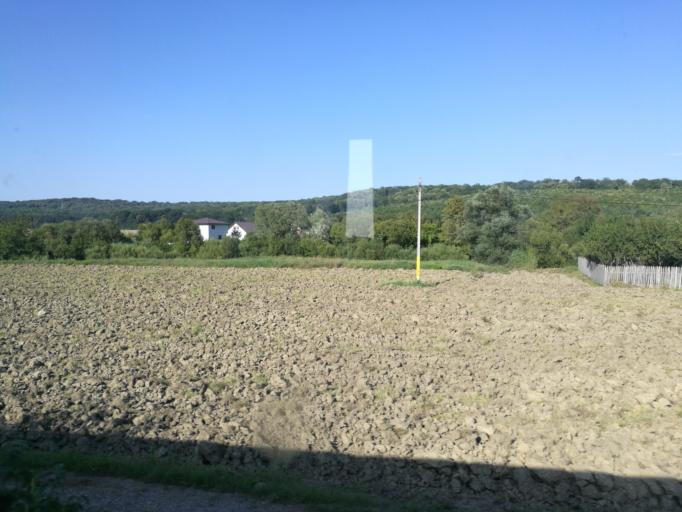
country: RO
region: Iasi
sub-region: Comuna Grajduri
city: Grajduri
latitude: 46.9583
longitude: 27.5573
